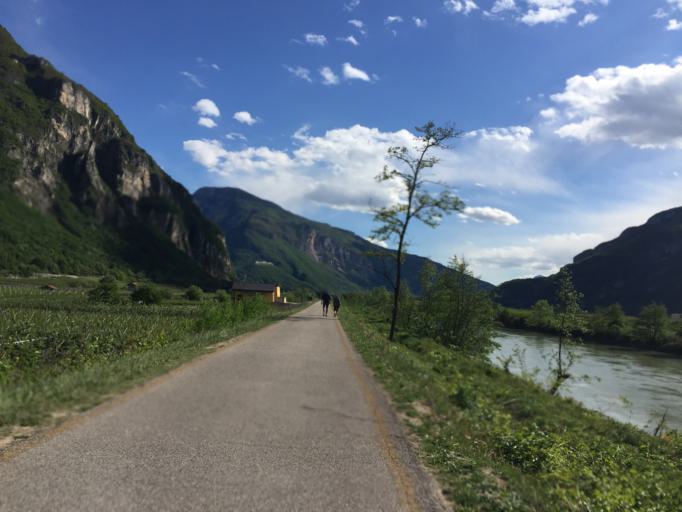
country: IT
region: Trentino-Alto Adige
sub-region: Provincia di Trento
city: Aldeno
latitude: 45.9723
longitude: 11.1090
